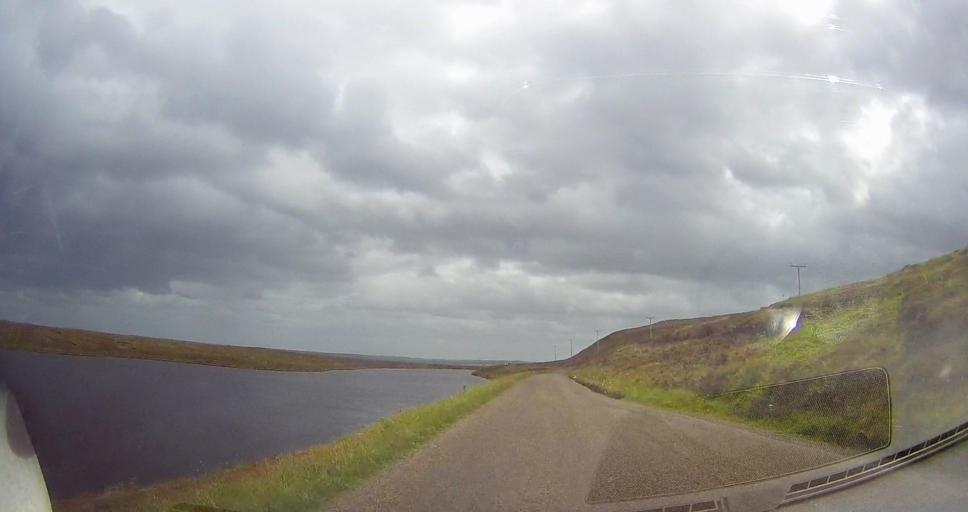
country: GB
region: Scotland
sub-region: Highland
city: Thurso
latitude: 58.6638
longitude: -3.3744
